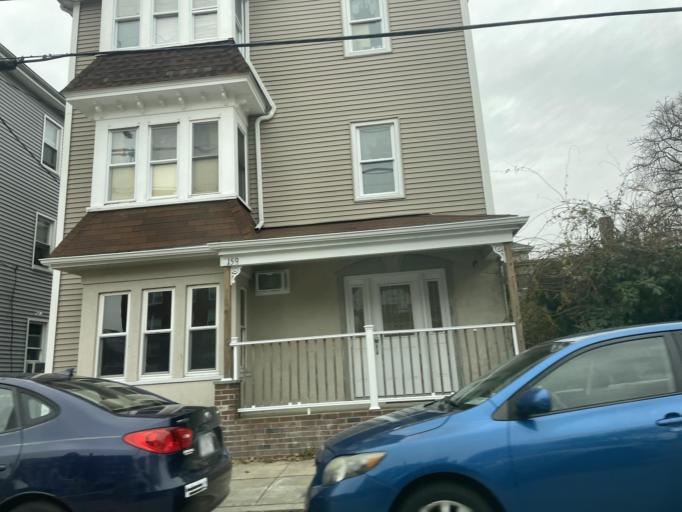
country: US
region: Massachusetts
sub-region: Bristol County
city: Fall River
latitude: 41.6920
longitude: -71.1338
